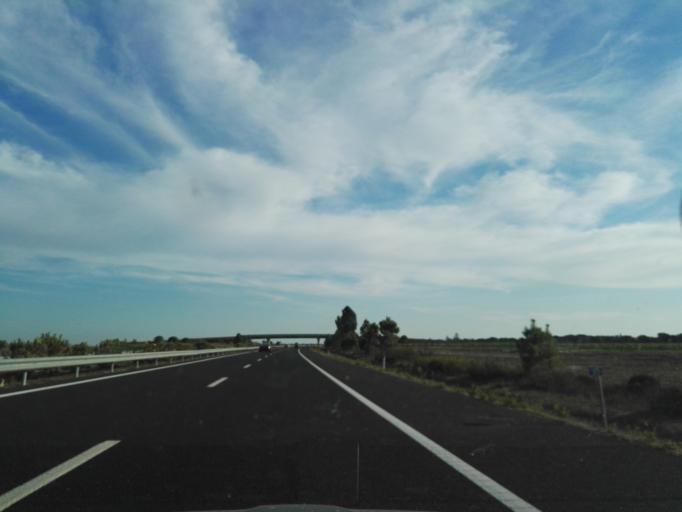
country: PT
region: Santarem
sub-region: Benavente
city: Poceirao
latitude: 38.7788
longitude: -8.6843
